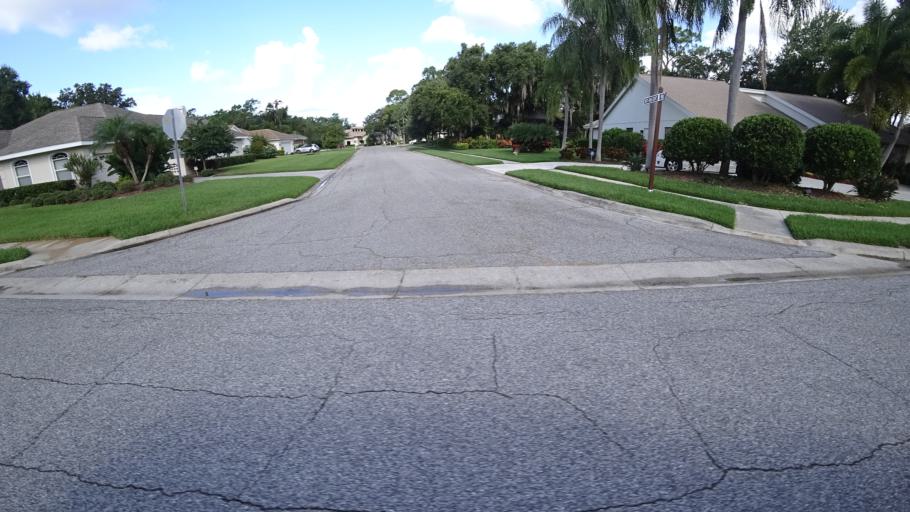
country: US
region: Florida
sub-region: Sarasota County
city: Desoto Lakes
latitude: 27.3960
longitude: -82.4827
